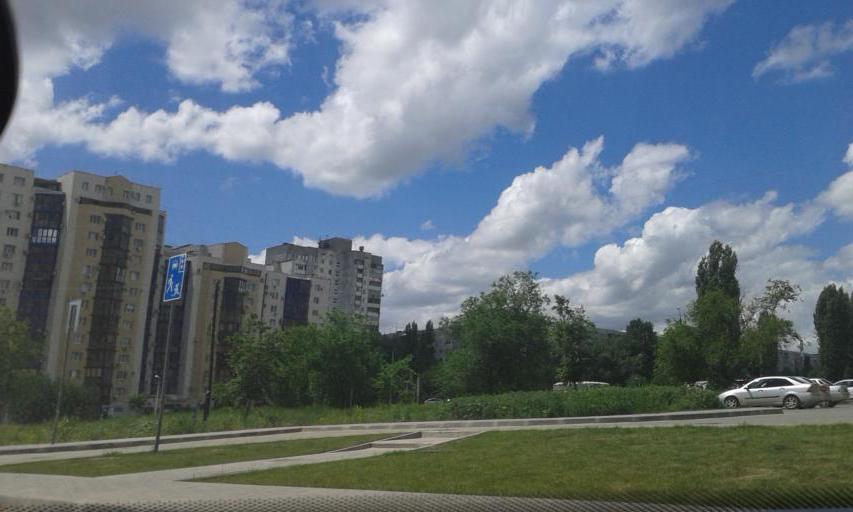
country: RU
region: Volgograd
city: Volgograd
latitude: 48.7486
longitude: 44.5081
